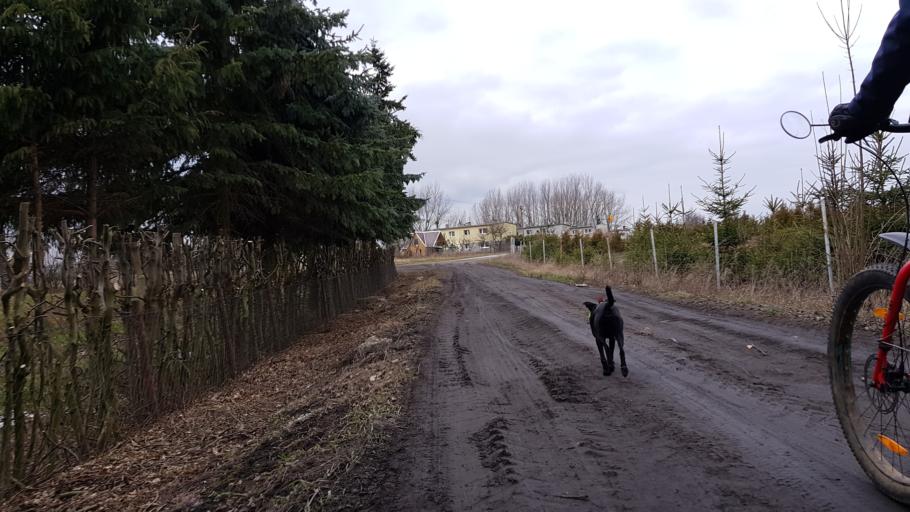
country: PL
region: West Pomeranian Voivodeship
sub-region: Powiat gryfinski
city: Banie
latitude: 53.0939
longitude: 14.7080
